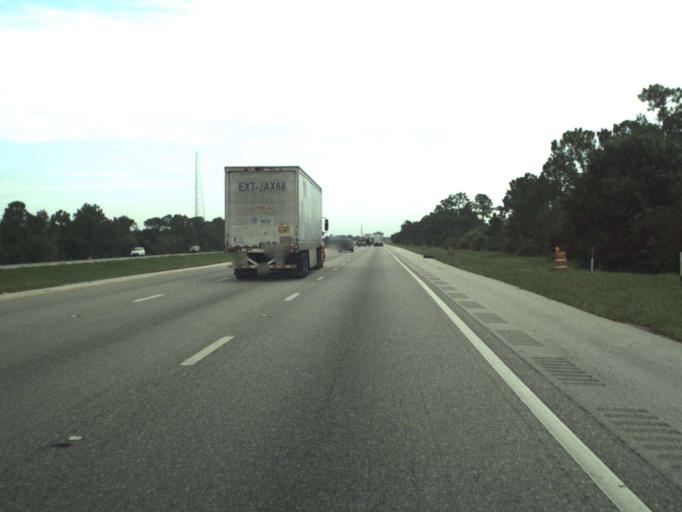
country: US
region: Florida
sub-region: Martin County
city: Port Salerno
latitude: 27.0775
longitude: -80.2480
